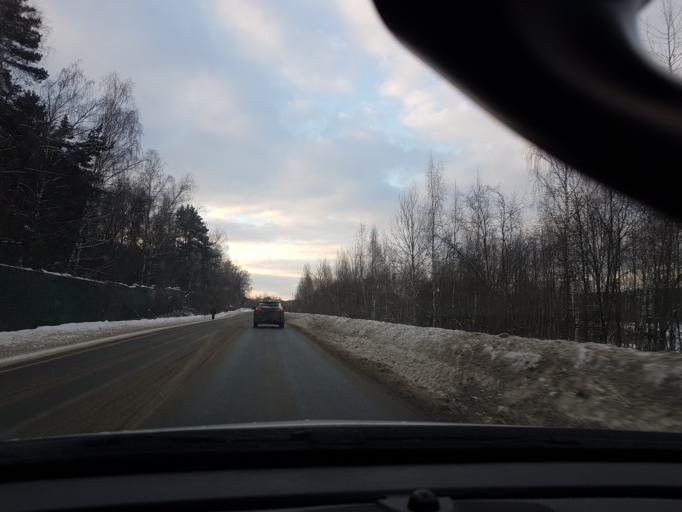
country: RU
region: Moskovskaya
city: Snegiri
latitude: 55.8449
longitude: 36.9605
